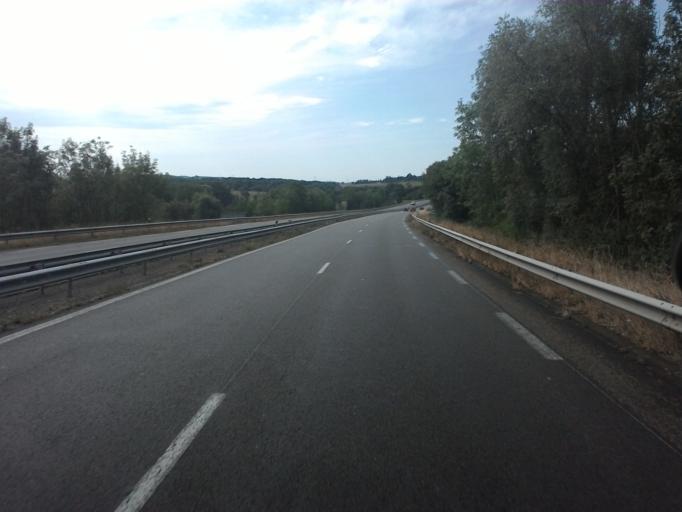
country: FR
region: Franche-Comte
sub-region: Departement du Jura
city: Lons-le-Saunier
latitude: 46.7342
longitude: 5.5582
